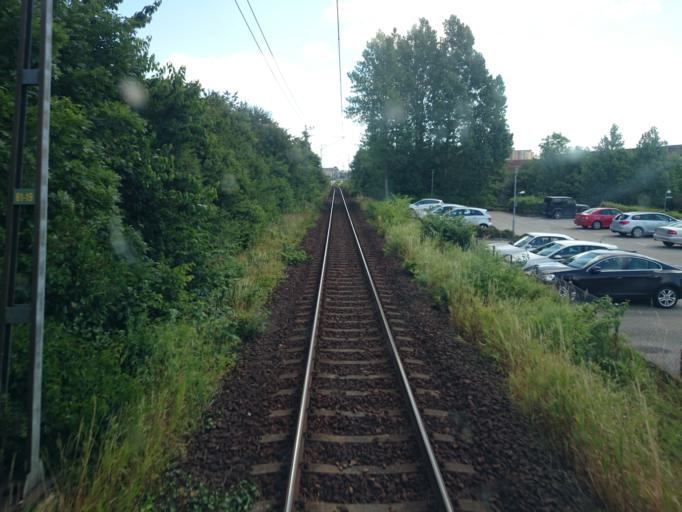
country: SE
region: Skane
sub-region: Ystads Kommun
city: Ystad
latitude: 55.4264
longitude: 13.8075
